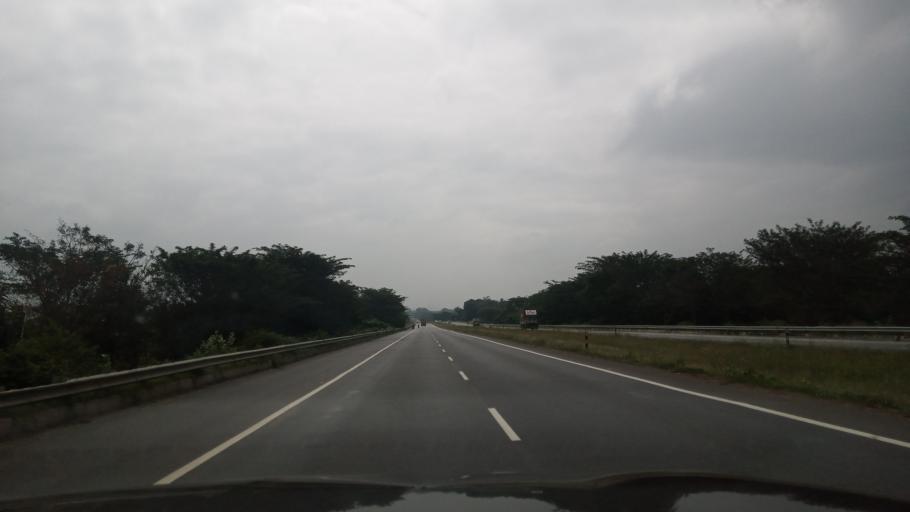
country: IN
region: Karnataka
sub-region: Bangalore Urban
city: Bangalore
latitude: 12.9435
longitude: 77.4699
